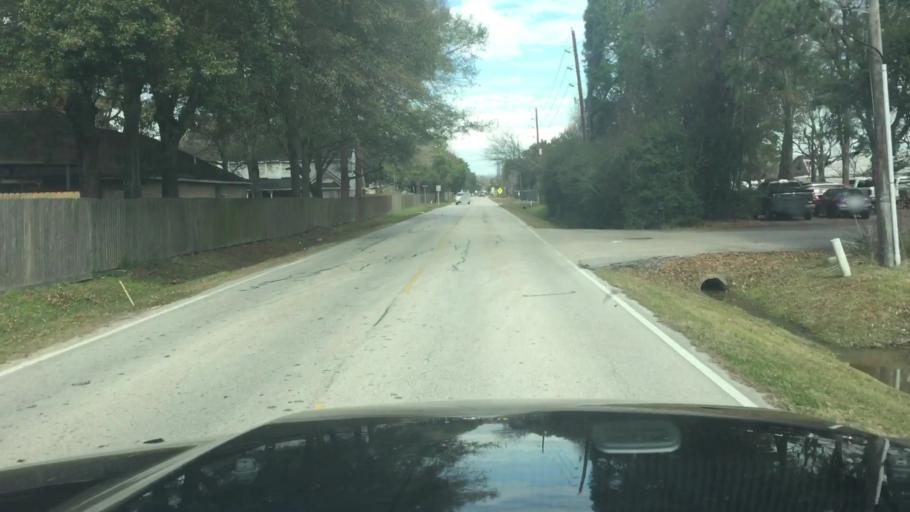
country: US
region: Texas
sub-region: Harris County
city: Oak Cliff Place
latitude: 29.8442
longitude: -95.6752
